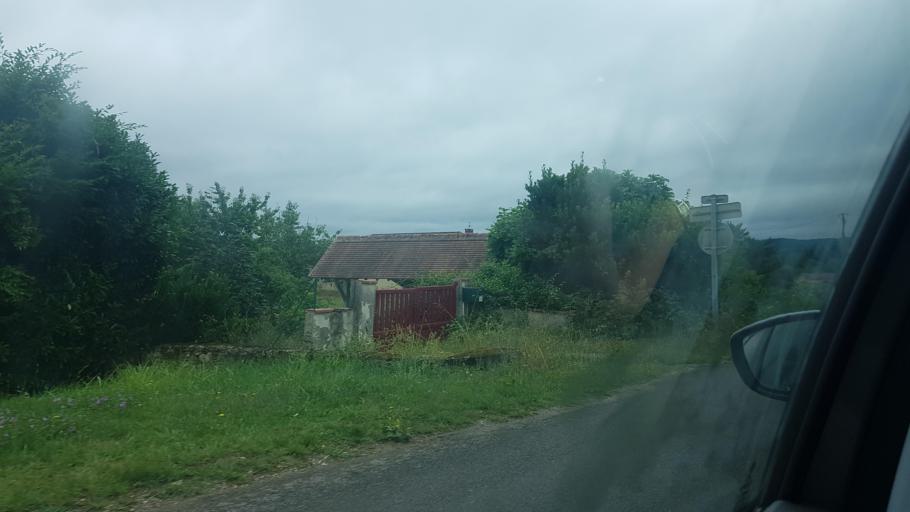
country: FR
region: Aquitaine
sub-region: Departement du Lot-et-Garonne
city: Montayral
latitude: 44.5137
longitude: 1.0787
